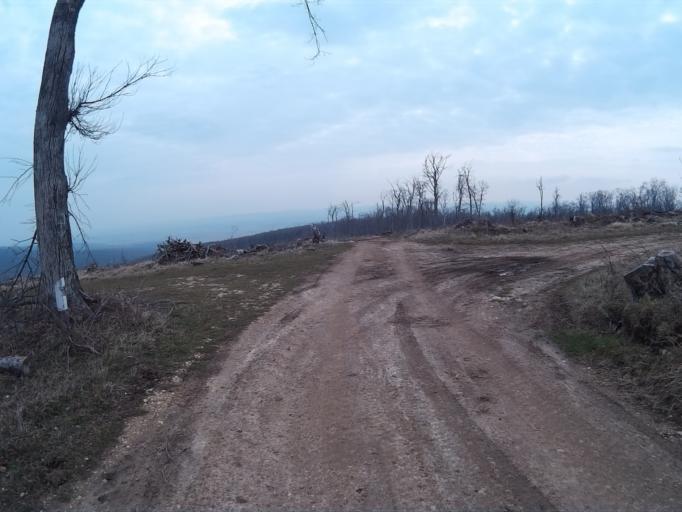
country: HU
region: Veszprem
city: Zirc
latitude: 47.1749
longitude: 17.8538
